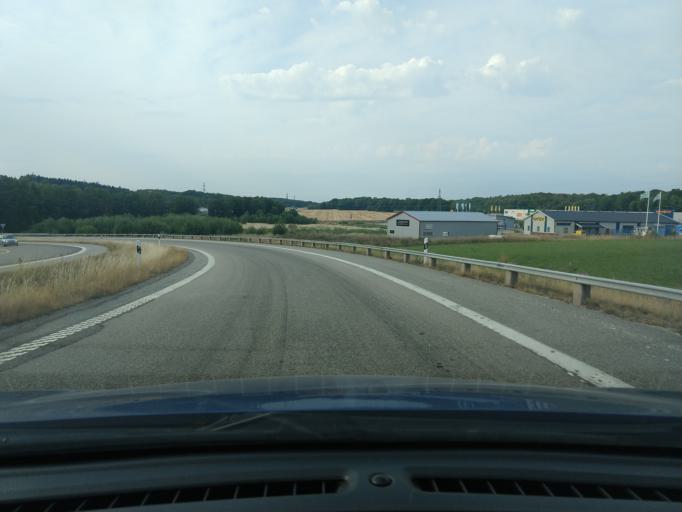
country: SE
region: Blekinge
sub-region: Ronneby Kommun
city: Kallinge
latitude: 56.2306
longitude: 15.2632
